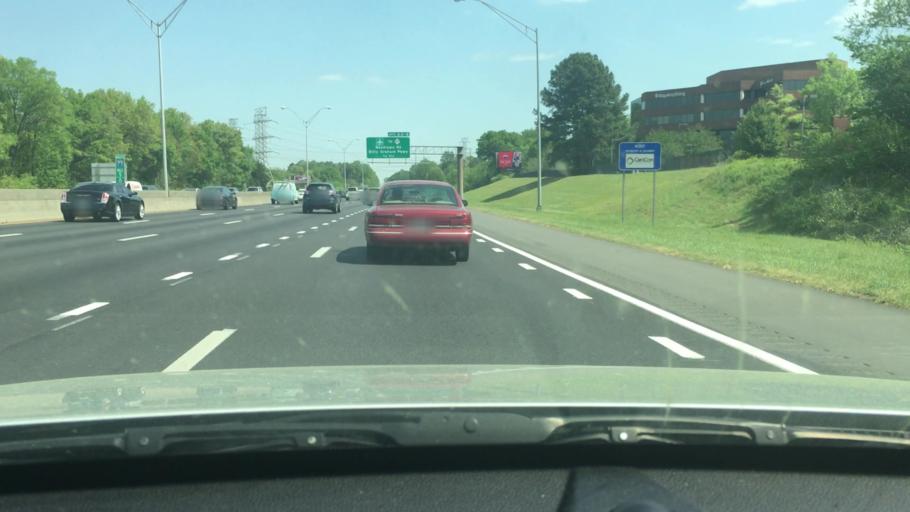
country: US
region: North Carolina
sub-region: Mecklenburg County
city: Charlotte
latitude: 35.1677
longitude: -80.8884
